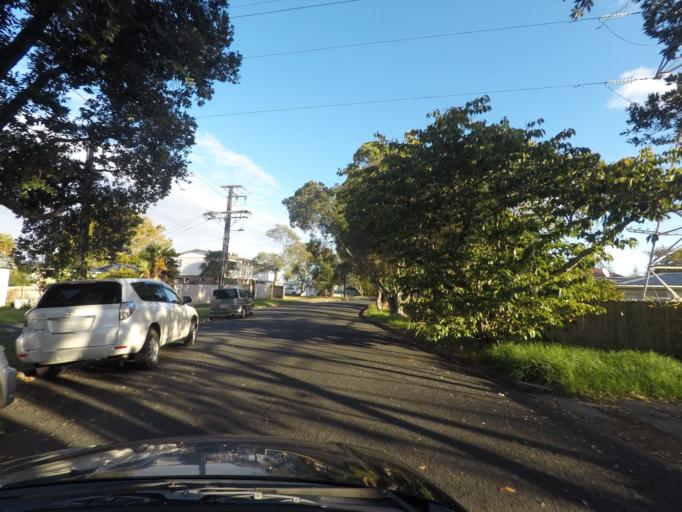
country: NZ
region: Auckland
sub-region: Auckland
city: Rosebank
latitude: -36.8995
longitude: 174.6769
